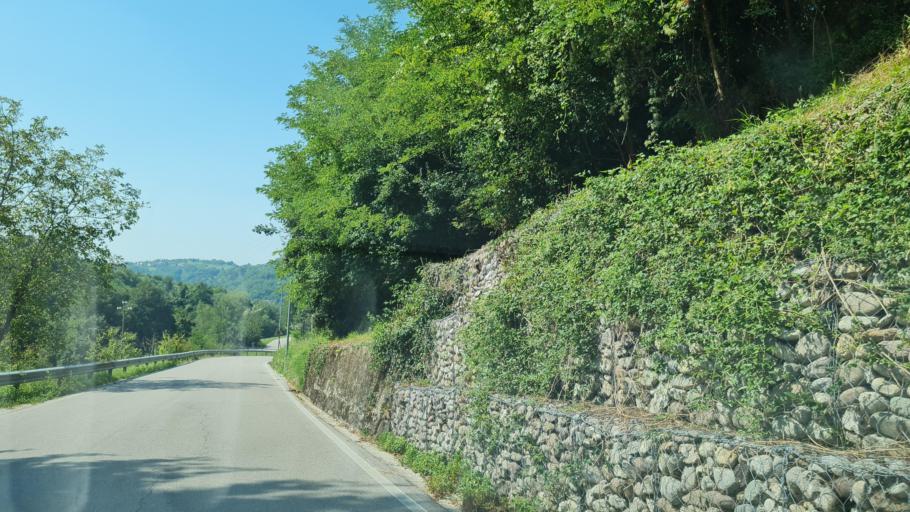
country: IT
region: Veneto
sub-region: Provincia di Vicenza
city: Salcedo
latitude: 45.7574
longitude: 11.5925
